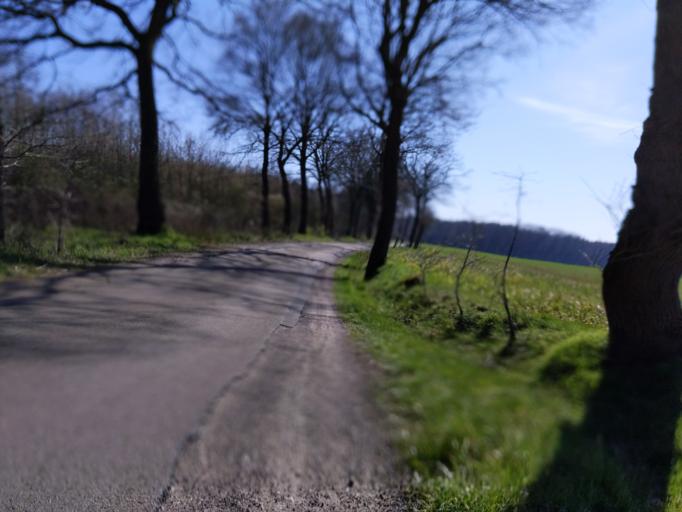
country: DE
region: North Rhine-Westphalia
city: Dorsten
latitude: 51.6969
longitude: 6.9756
